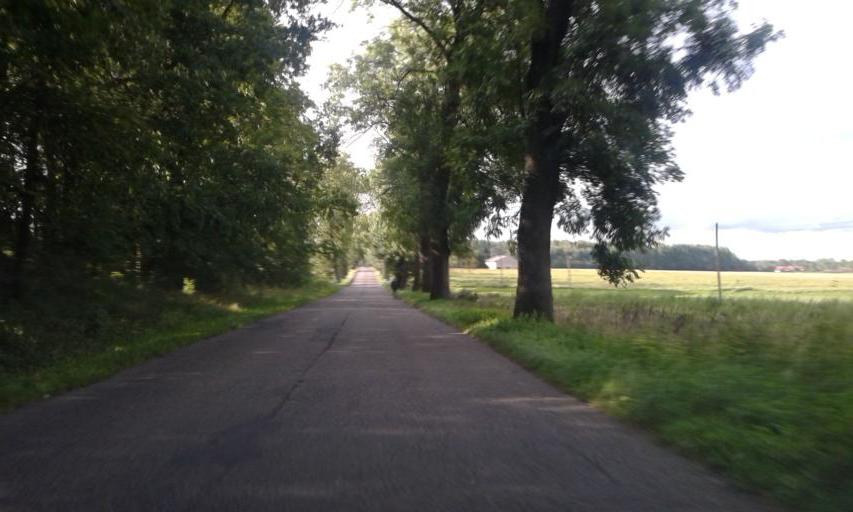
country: PL
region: West Pomeranian Voivodeship
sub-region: Powiat bialogardzki
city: Tychowo
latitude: 53.9102
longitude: 16.2422
